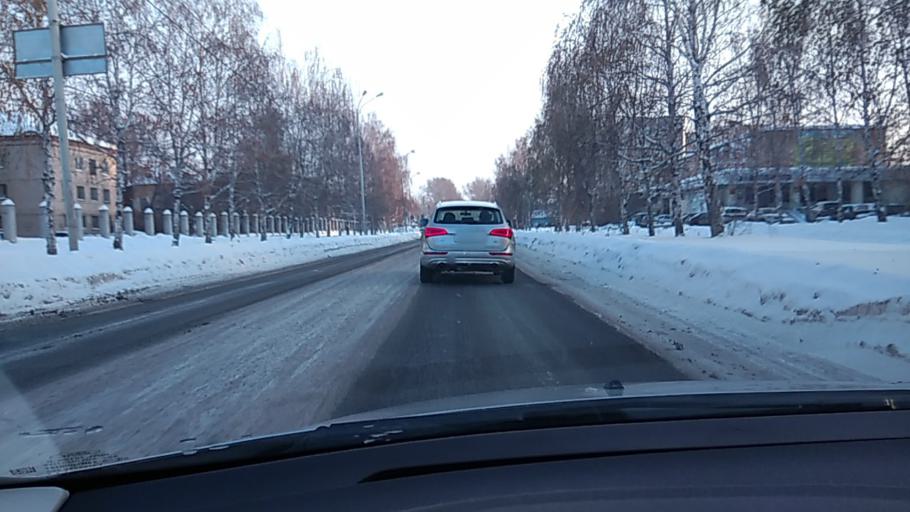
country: RU
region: Sverdlovsk
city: Yekaterinburg
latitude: 56.8125
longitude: 60.5757
